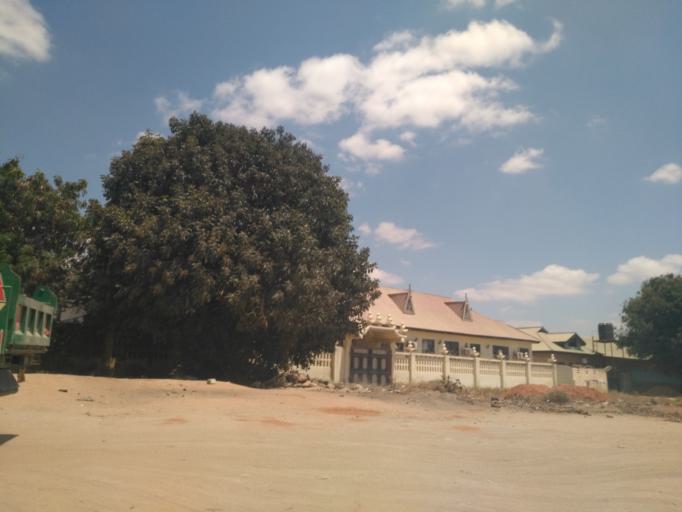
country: TZ
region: Dodoma
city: Dodoma
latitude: -6.1743
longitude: 35.7534
